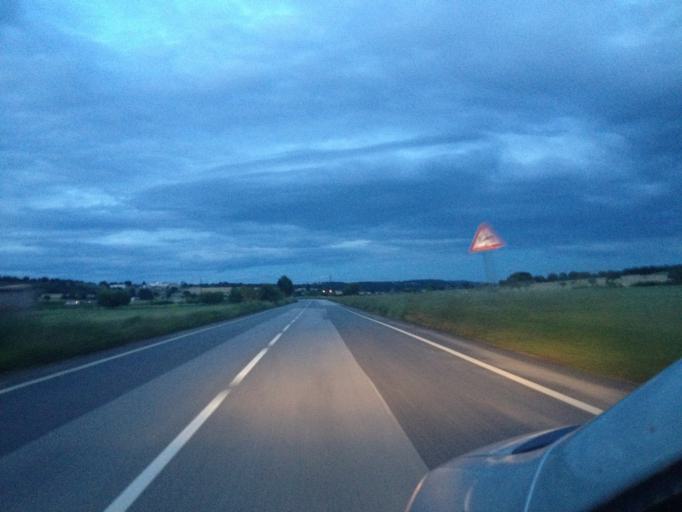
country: IT
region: Apulia
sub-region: Provincia di Bari
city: Alberobello
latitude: 40.8247
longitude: 17.2305
